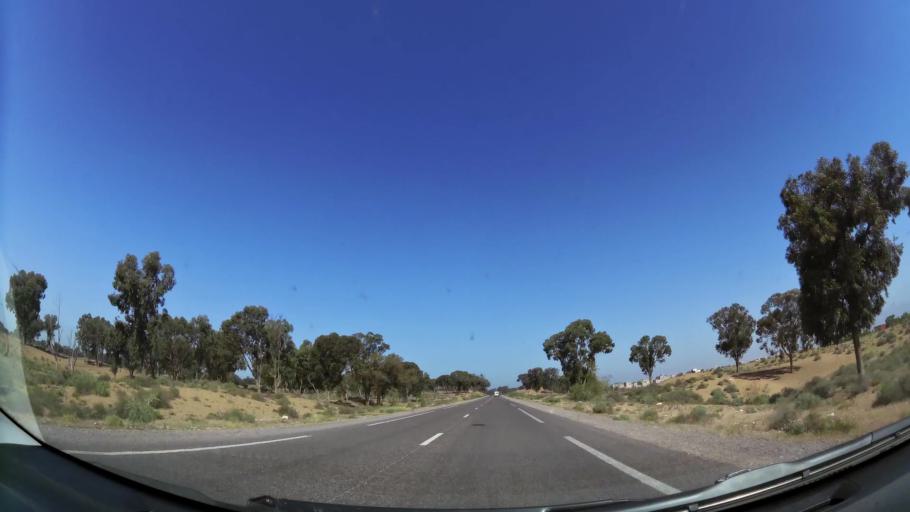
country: MA
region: Souss-Massa-Draa
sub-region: Inezgane-Ait Mellou
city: Inezgane
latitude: 30.3146
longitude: -9.5216
